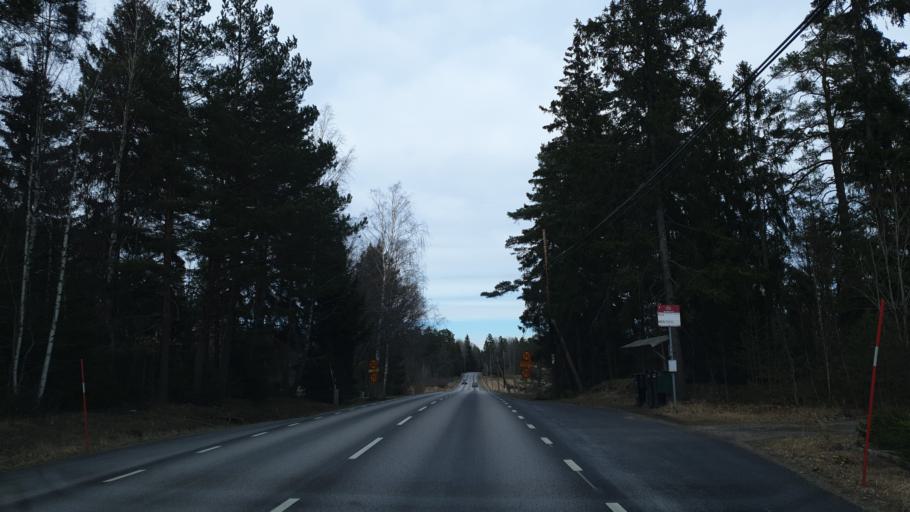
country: SE
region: Stockholm
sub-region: Osterakers Kommun
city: Akersberga
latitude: 59.5759
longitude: 18.2780
